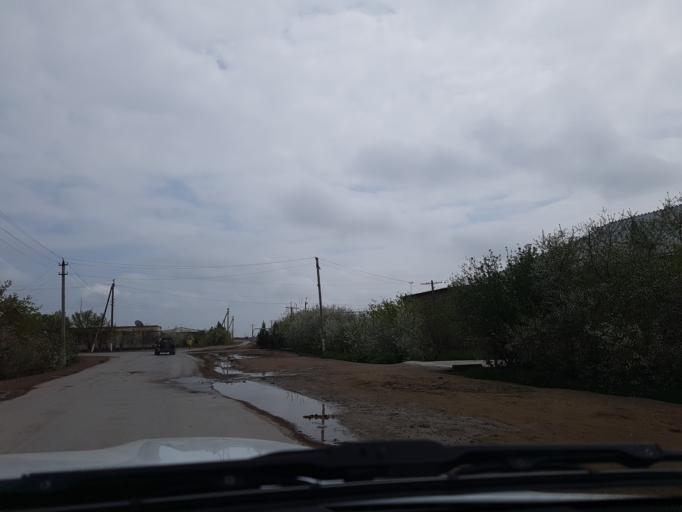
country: TM
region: Lebap
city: Turkmenabat
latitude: 38.9712
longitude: 63.6854
